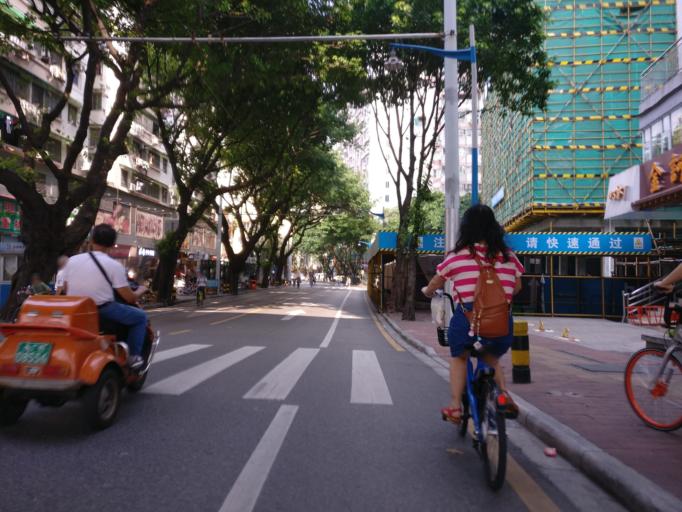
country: CN
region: Guangdong
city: Guangzhou
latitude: 23.1252
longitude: 113.2732
